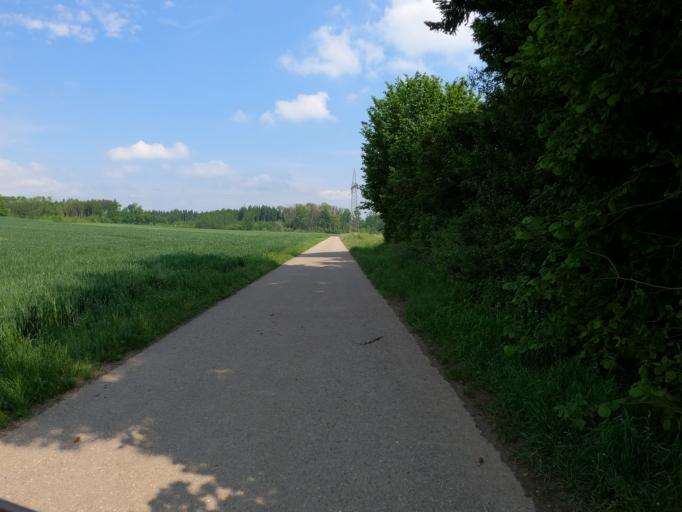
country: DE
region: Bavaria
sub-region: Swabia
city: Holzheim
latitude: 48.3858
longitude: 10.1011
